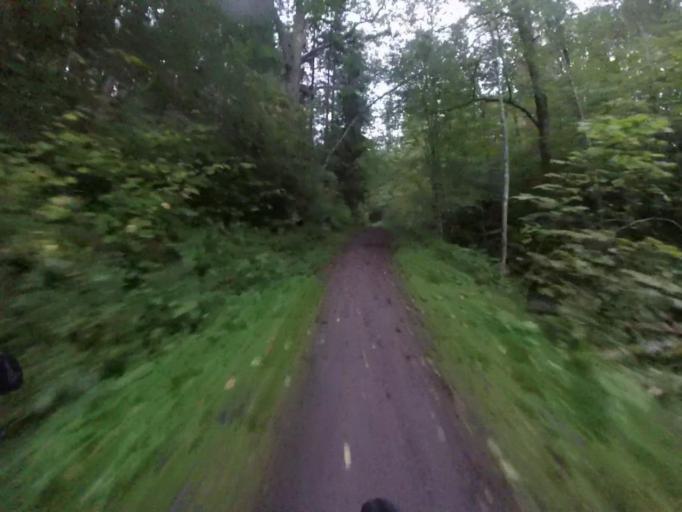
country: SE
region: Vaestra Goetaland
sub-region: Trollhattan
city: Trollhattan
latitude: 58.2775
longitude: 12.2577
